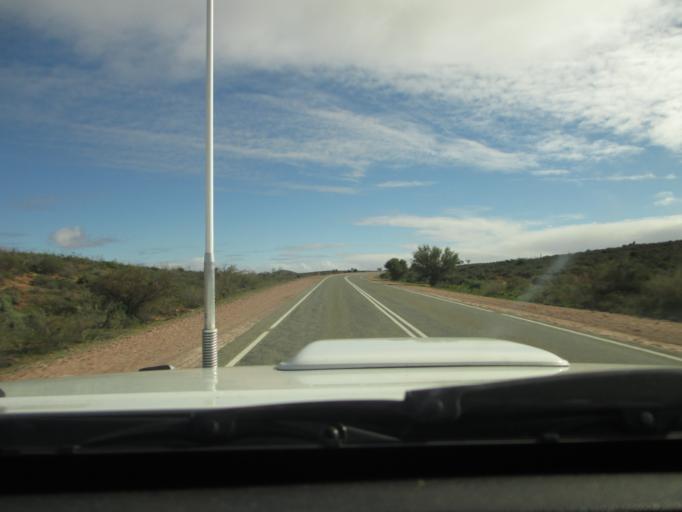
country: AU
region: South Australia
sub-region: Flinders Ranges
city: Quorn
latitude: -31.8137
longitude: 138.3704
